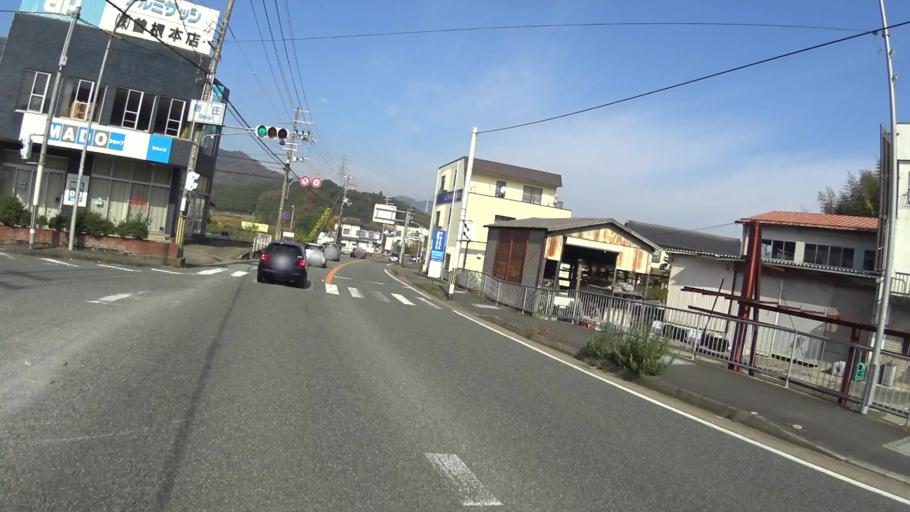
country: JP
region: Kyoto
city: Fukuchiyama
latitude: 35.3052
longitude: 135.1037
